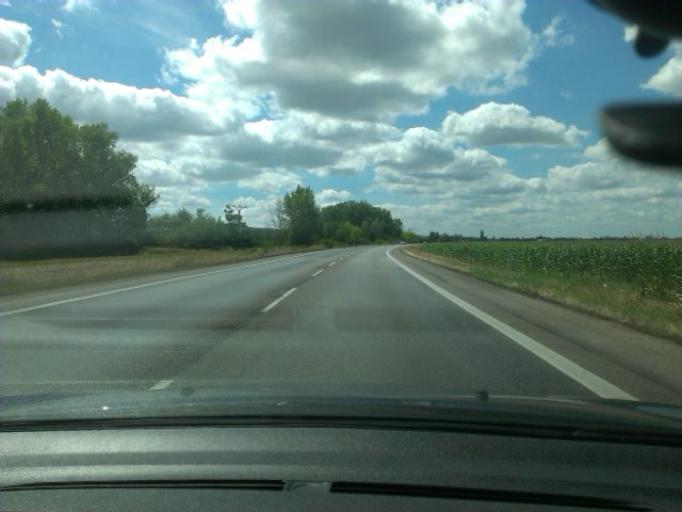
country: SK
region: Trnavsky
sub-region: Okres Trnava
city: Piestany
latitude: 48.6326
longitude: 17.8394
